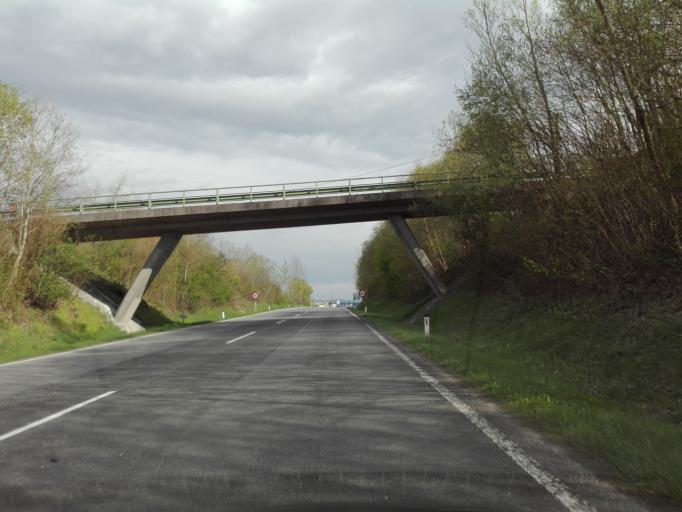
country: AT
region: Upper Austria
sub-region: Politischer Bezirk Rohrbach
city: Kleinzell im Muehlkreis
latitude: 48.4868
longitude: 13.9763
